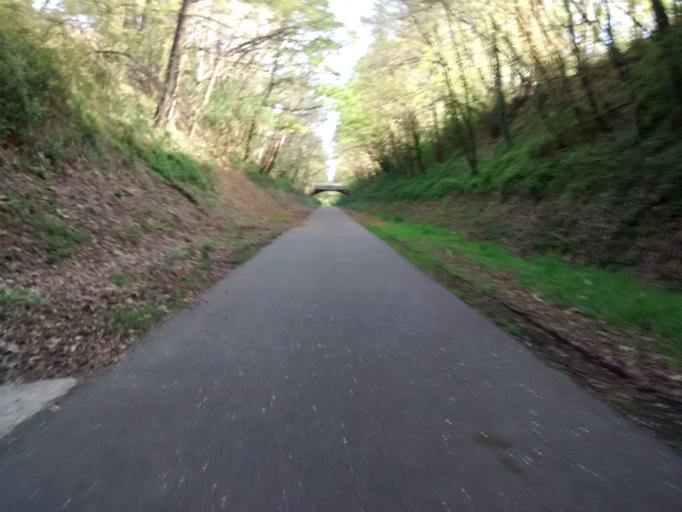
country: FR
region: Brittany
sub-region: Departement du Morbihan
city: Malestroit
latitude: 47.8018
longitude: -2.3988
